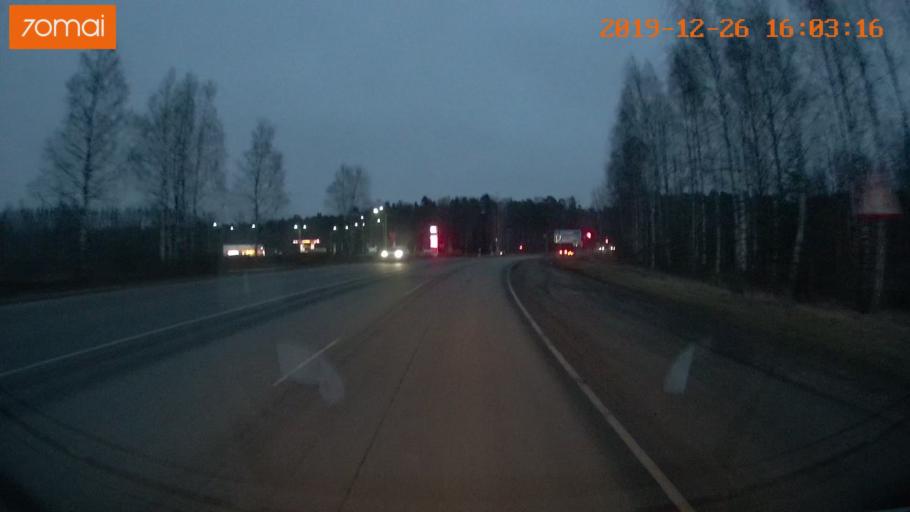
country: RU
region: Jaroslavl
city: Rybinsk
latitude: 58.0111
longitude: 38.8552
